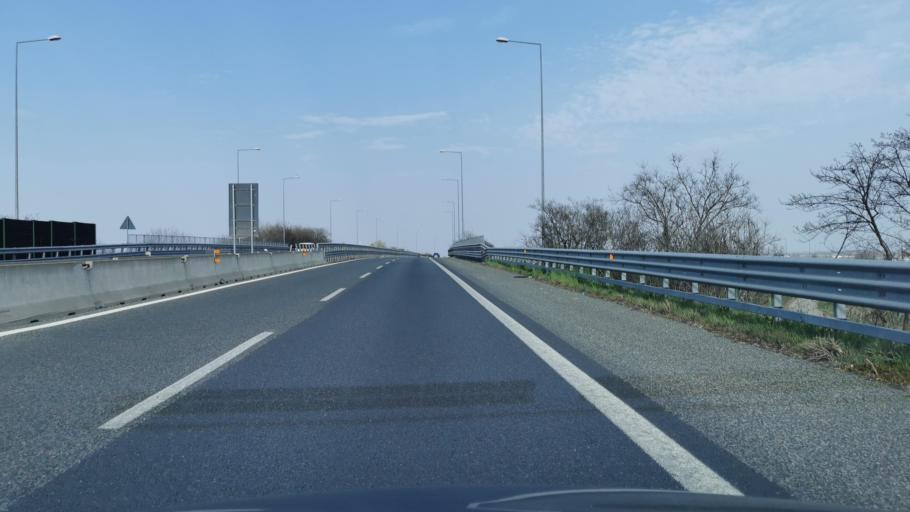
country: IT
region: Piedmont
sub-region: Provincia di Torino
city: Riva
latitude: 44.8937
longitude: 7.3999
